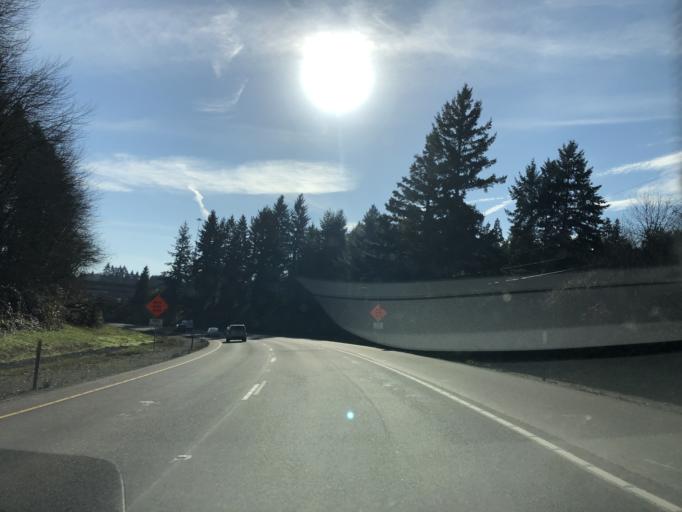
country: US
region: Oregon
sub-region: Washington County
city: Tualatin
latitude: 45.3713
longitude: -122.7590
